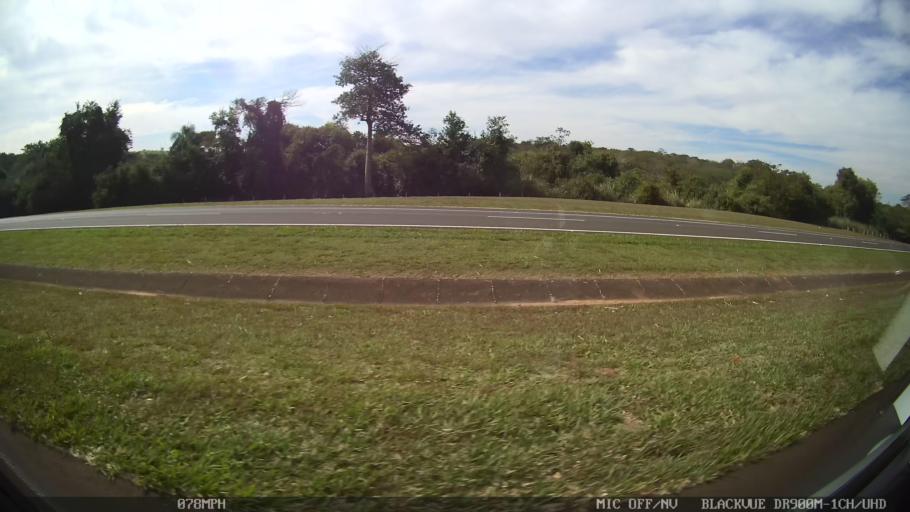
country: BR
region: Sao Paulo
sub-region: Matao
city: Matao
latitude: -21.6150
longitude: -48.4192
